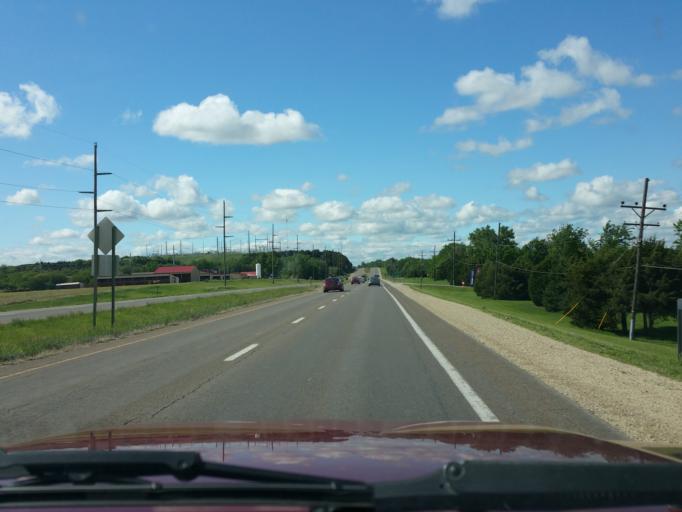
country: US
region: Kansas
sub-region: Riley County
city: Manhattan
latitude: 39.2252
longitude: -96.5823
